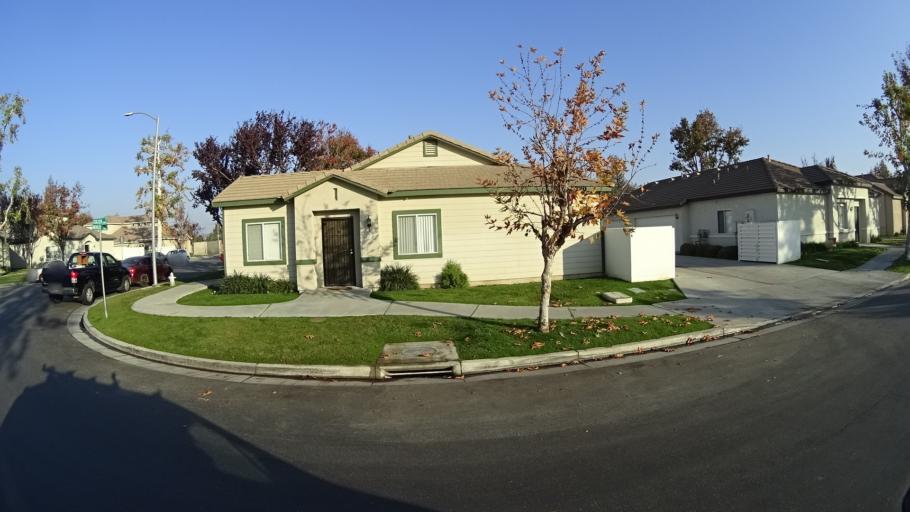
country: US
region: California
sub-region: Kern County
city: Rosedale
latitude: 35.3807
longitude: -119.1465
